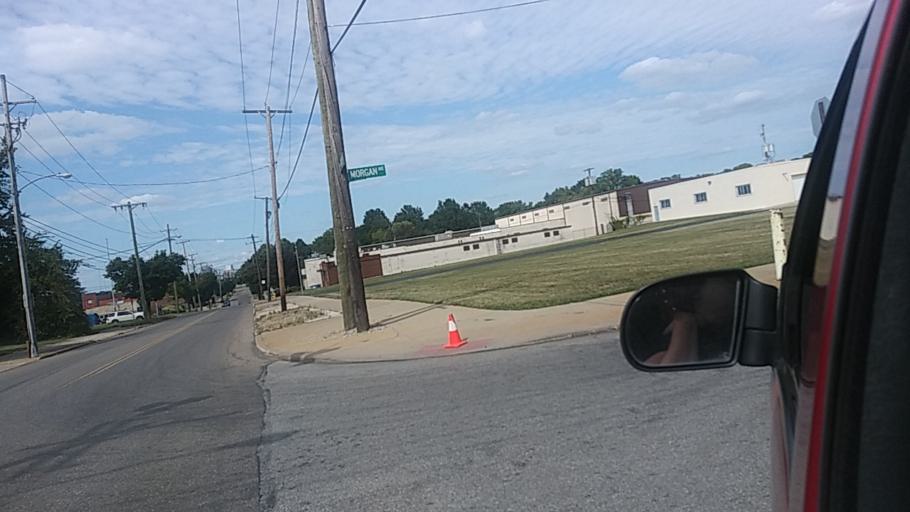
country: US
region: Ohio
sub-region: Summit County
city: Akron
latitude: 41.0554
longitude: -81.5181
